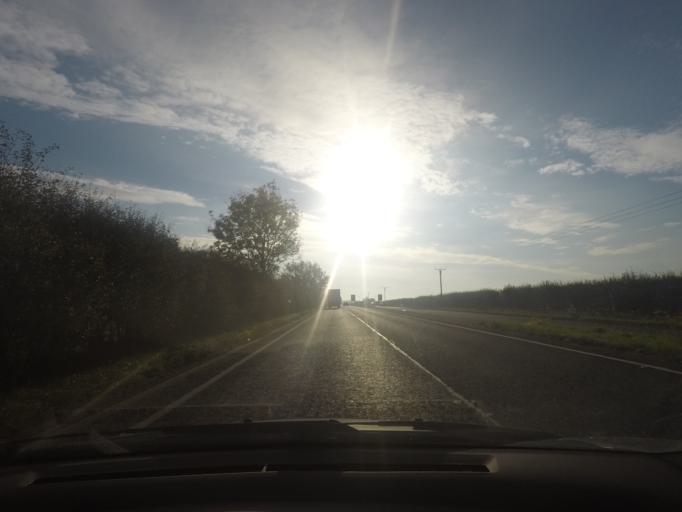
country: GB
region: England
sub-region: East Riding of Yorkshire
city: Hayton
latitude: 53.8970
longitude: -0.7460
